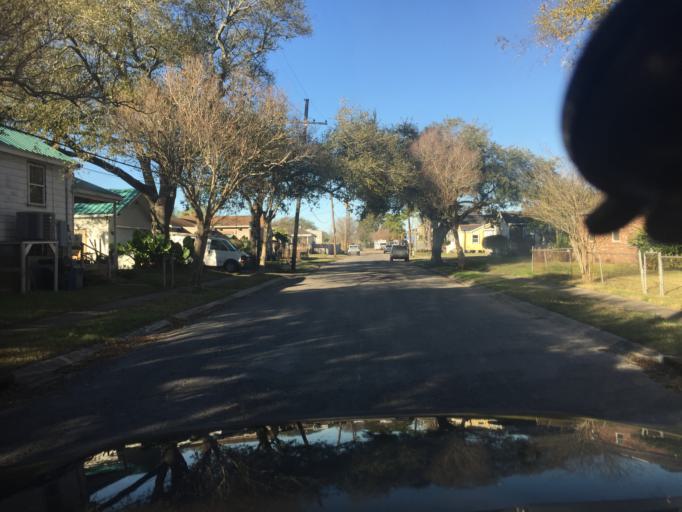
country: US
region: Louisiana
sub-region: Orleans Parish
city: New Orleans
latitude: 29.9890
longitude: -90.0807
